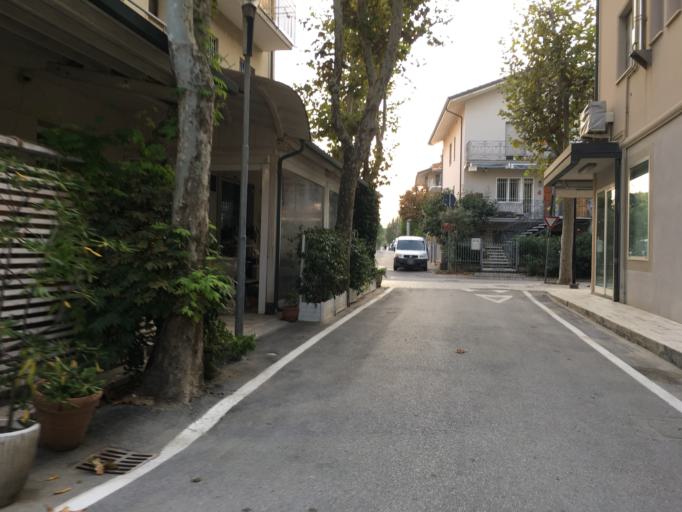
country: IT
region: Emilia-Romagna
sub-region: Forli-Cesena
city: San Mauro a Mare
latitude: 44.1635
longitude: 12.4482
